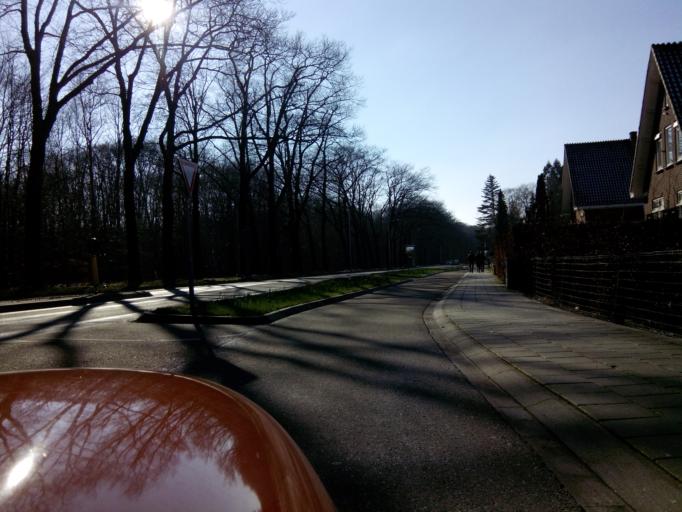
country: NL
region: Gelderland
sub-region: Gemeente Barneveld
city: Barneveld
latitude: 52.1530
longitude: 5.5966
